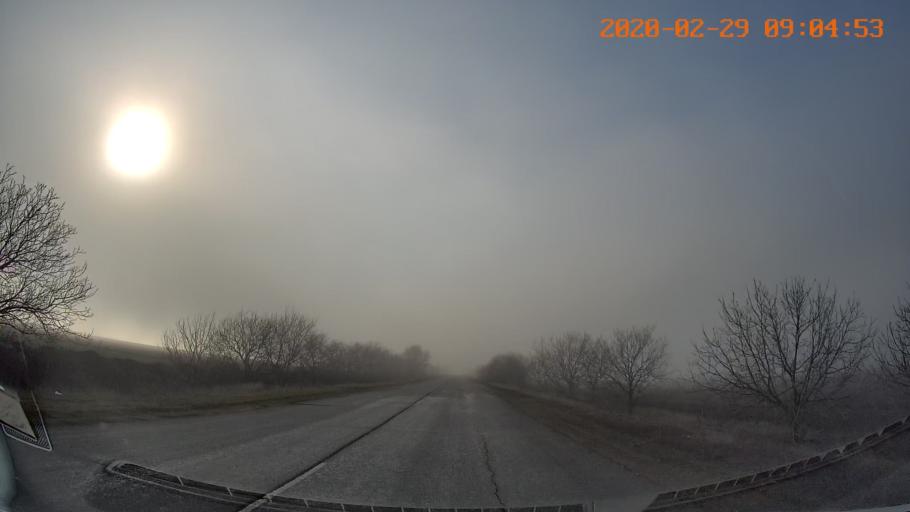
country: MD
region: Telenesti
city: Tiraspolul Nou
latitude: 46.8964
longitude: 29.7380
